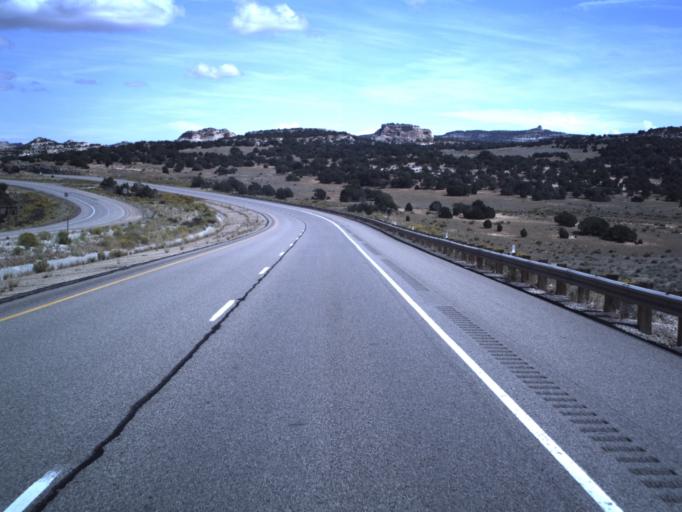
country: US
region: Utah
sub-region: Emery County
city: Ferron
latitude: 38.8471
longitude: -110.8967
